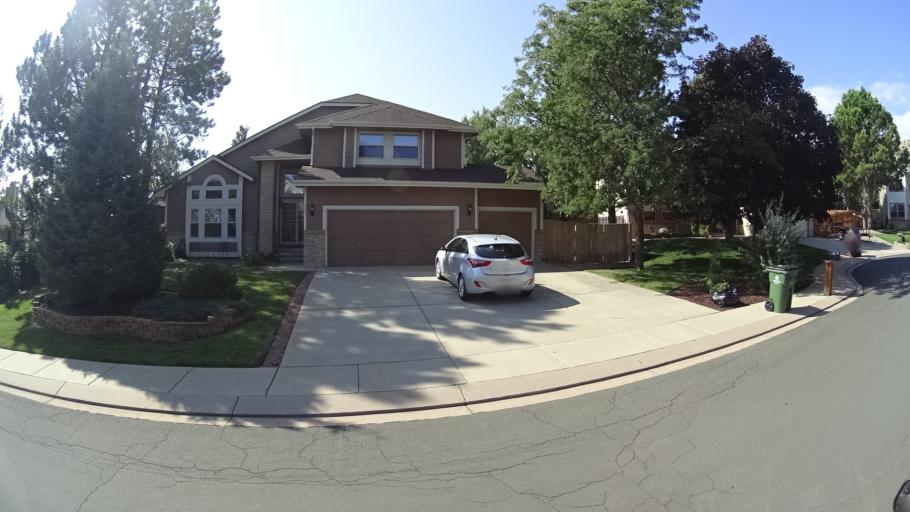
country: US
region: Colorado
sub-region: El Paso County
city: Manitou Springs
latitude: 38.9051
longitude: -104.8736
